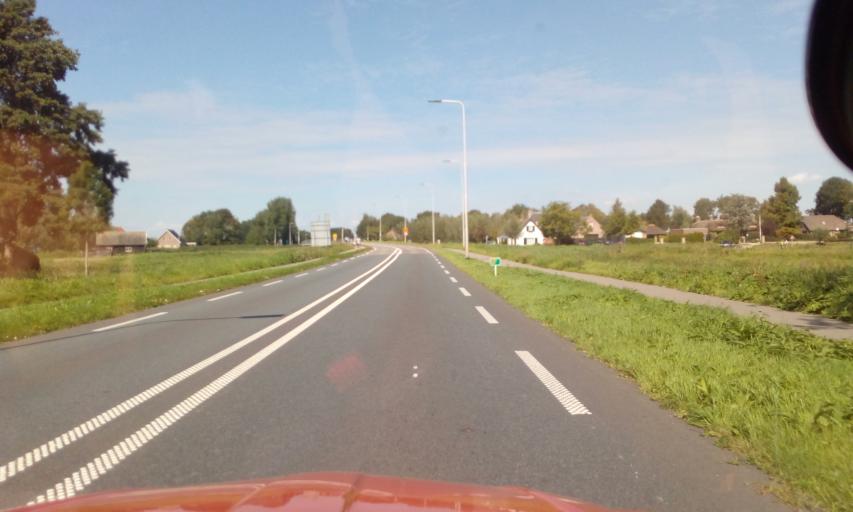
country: NL
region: South Holland
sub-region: Gemeente Giessenlanden
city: Giessenburg
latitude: 51.8653
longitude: 4.9041
